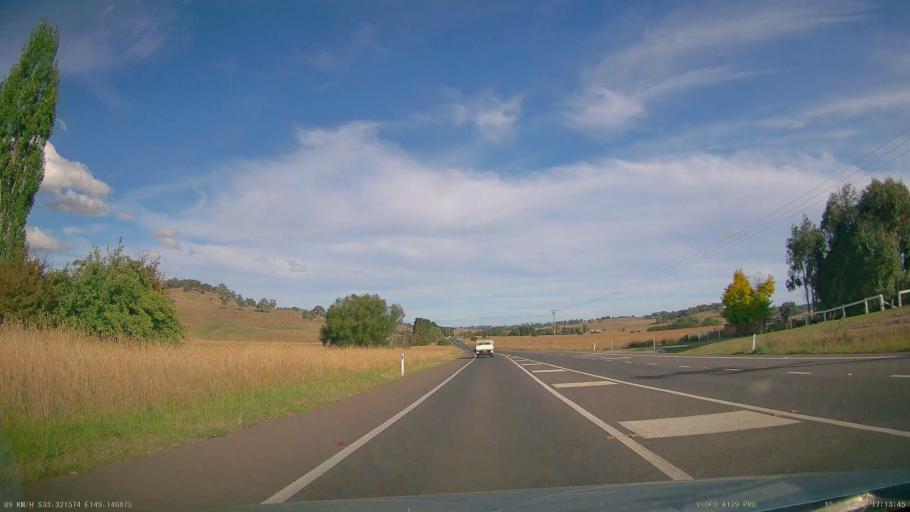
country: AU
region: New South Wales
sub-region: Orange Municipality
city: Orange
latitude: -33.3218
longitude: 149.1470
